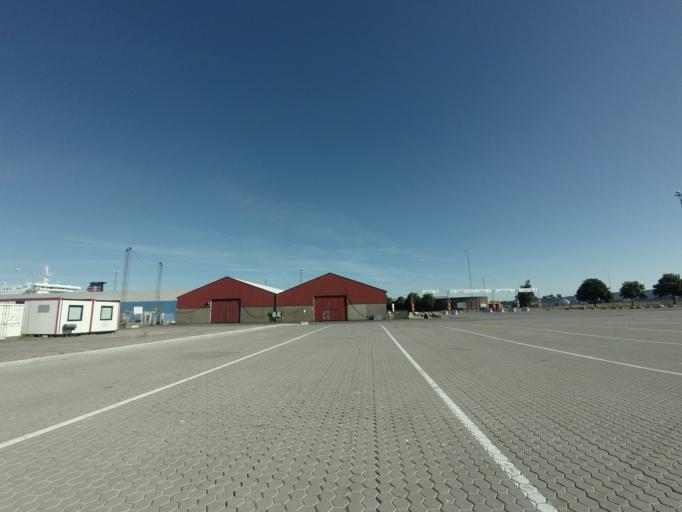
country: SE
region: Skane
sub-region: Ystads Kommun
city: Ystad
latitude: 55.4228
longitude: 13.8351
